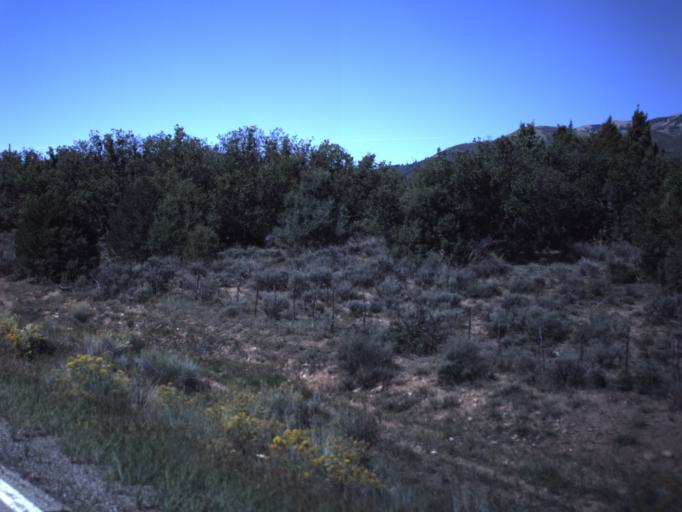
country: US
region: Utah
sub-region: Grand County
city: Moab
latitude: 38.3434
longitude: -109.2057
